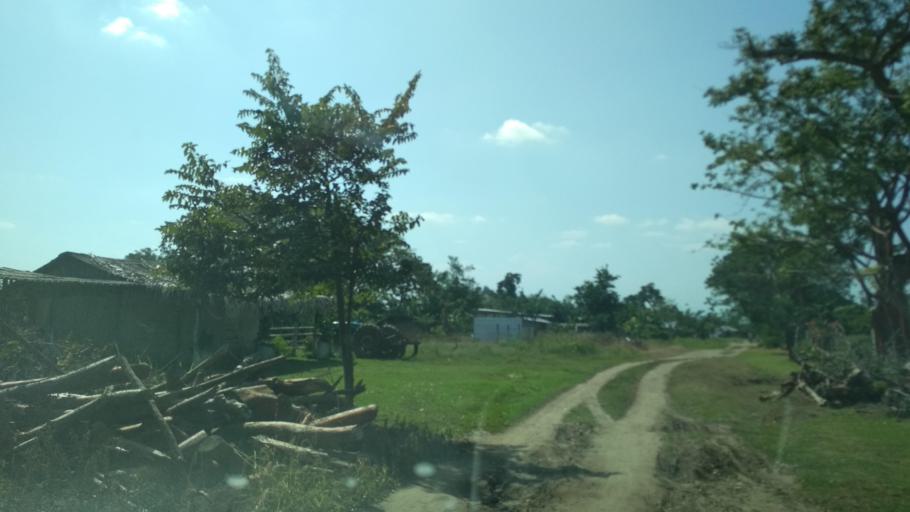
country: MX
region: Puebla
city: San Jose Acateno
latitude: 20.1645
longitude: -97.1652
